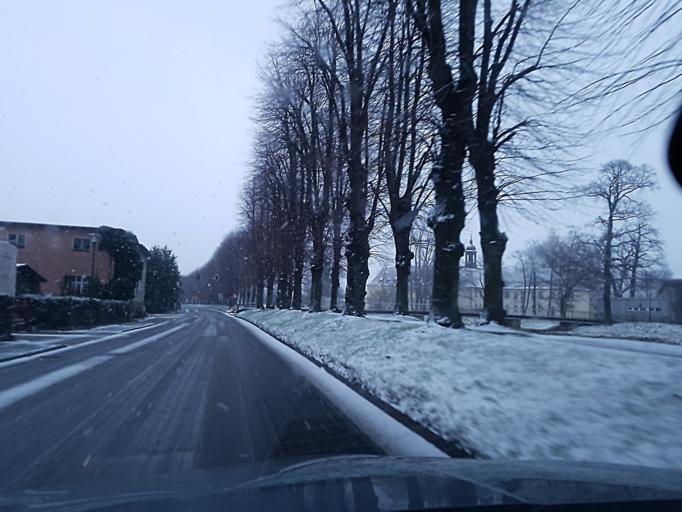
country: DE
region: Brandenburg
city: Elsterwerda
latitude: 51.4542
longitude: 13.5205
